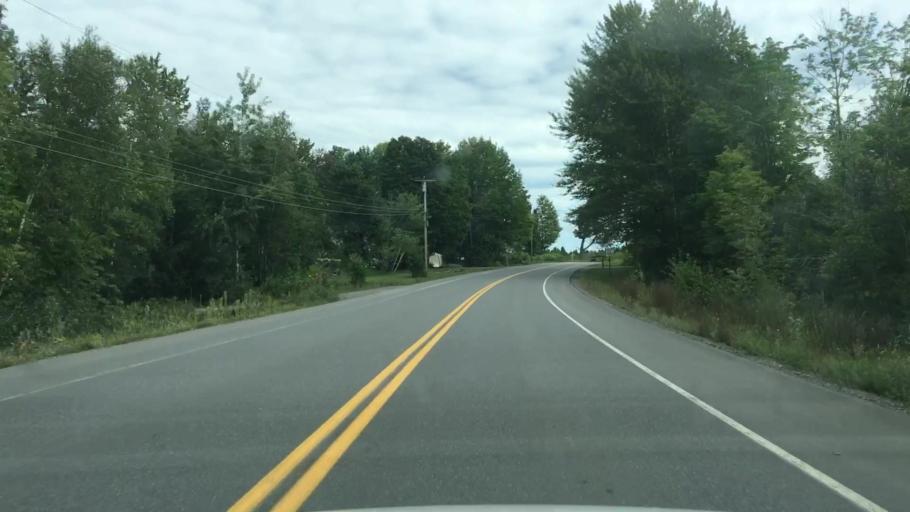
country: US
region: Maine
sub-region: Piscataquis County
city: Milo
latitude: 45.2395
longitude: -69.0471
